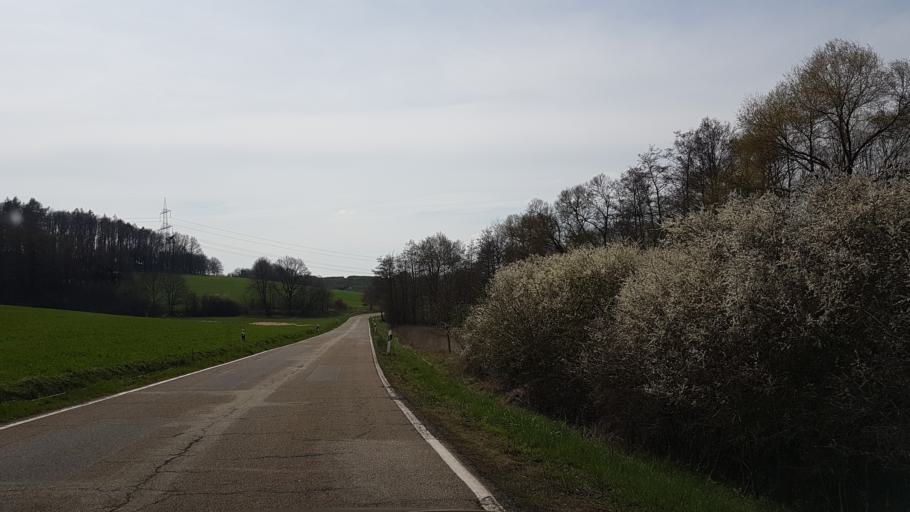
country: DE
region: Rheinland-Pfalz
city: Nanzdietschweiler
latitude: 49.4303
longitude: 7.4394
